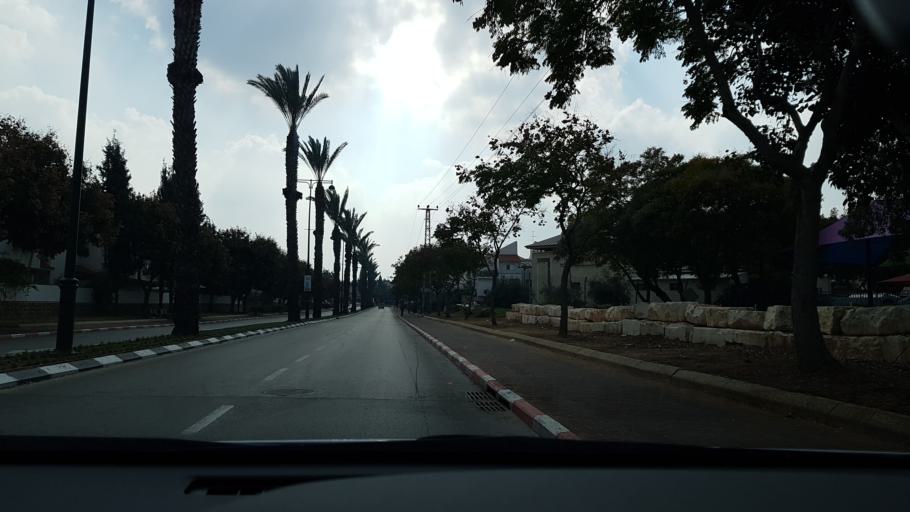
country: IL
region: Central District
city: Mazkeret Batya
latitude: 31.8684
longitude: 34.8198
